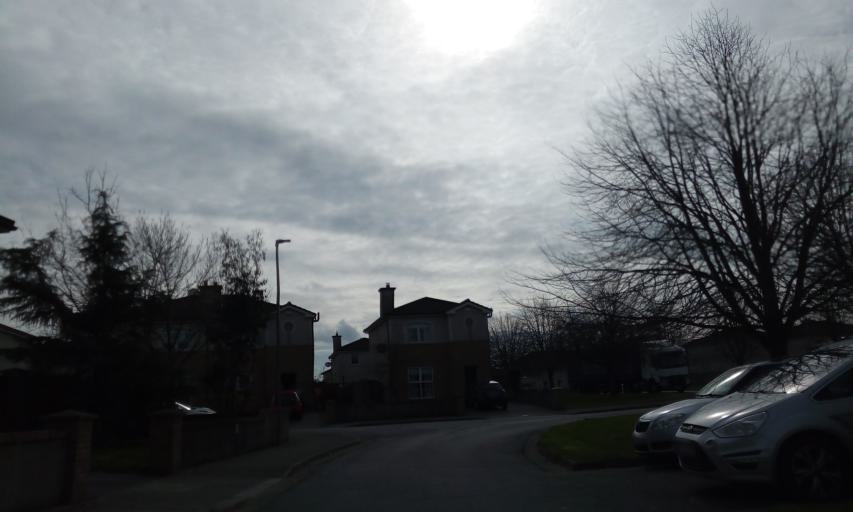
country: IE
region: Leinster
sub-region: Kilkenny
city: Kilkenny
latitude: 52.6672
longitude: -7.2348
